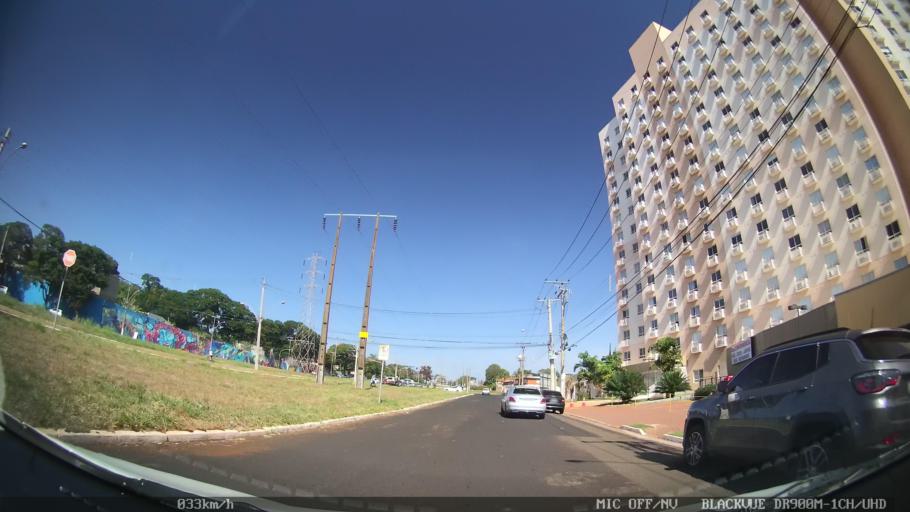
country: BR
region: Sao Paulo
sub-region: Ribeirao Preto
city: Ribeirao Preto
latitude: -21.1981
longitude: -47.7797
